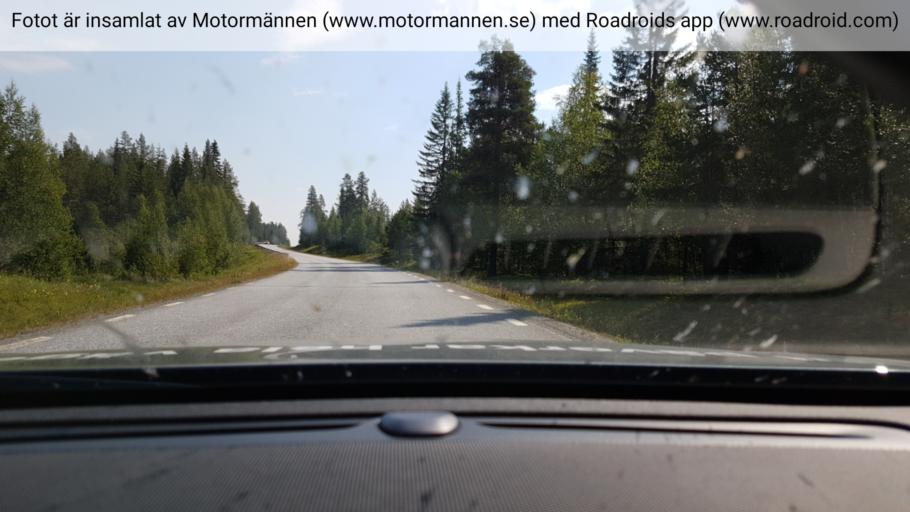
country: SE
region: Vaesterbotten
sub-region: Storumans Kommun
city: Fristad
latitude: 65.4049
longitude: 16.3545
